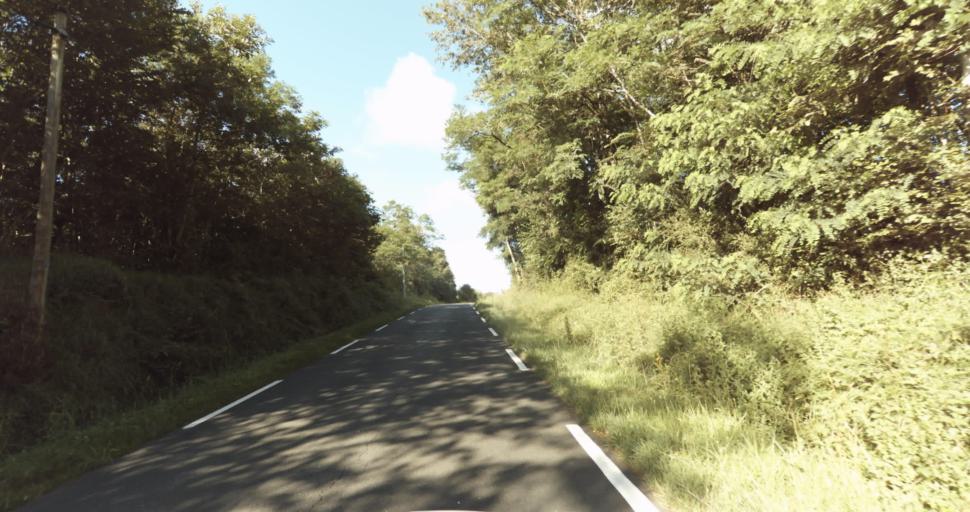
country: FR
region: Aquitaine
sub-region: Departement de la Gironde
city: Bazas
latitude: 44.4230
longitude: -0.2469
